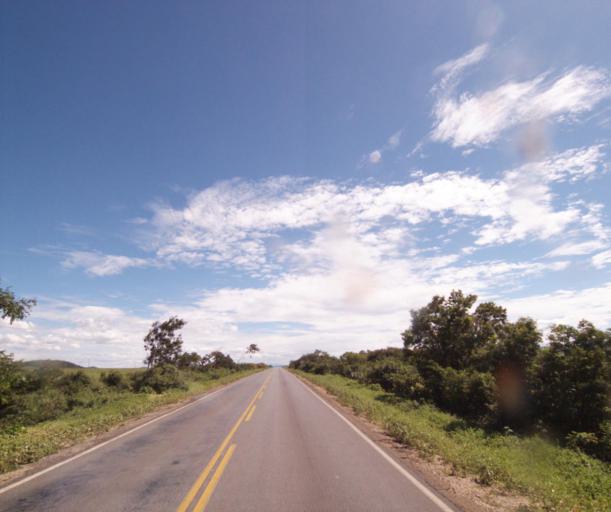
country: BR
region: Bahia
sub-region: Guanambi
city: Guanambi
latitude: -14.5356
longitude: -42.6979
